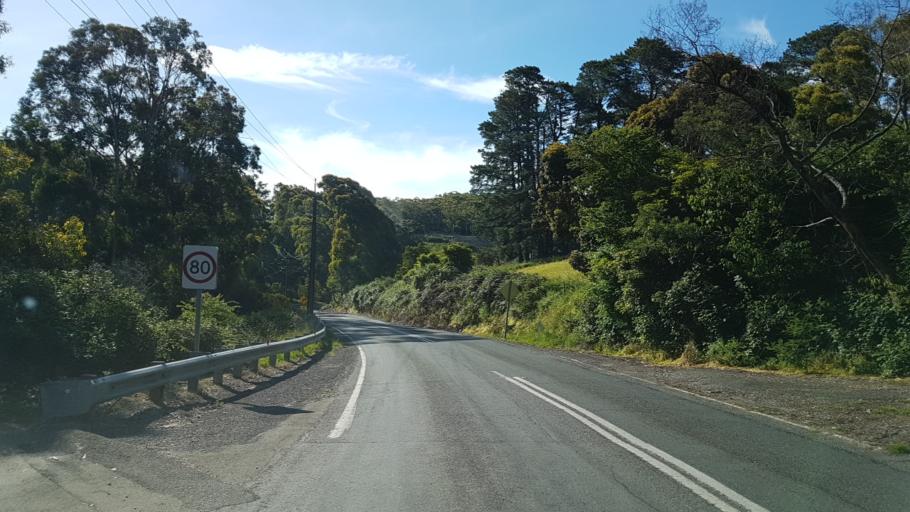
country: AU
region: South Australia
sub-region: Adelaide Hills
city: Adelaide Hills
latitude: -34.9397
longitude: 138.7368
